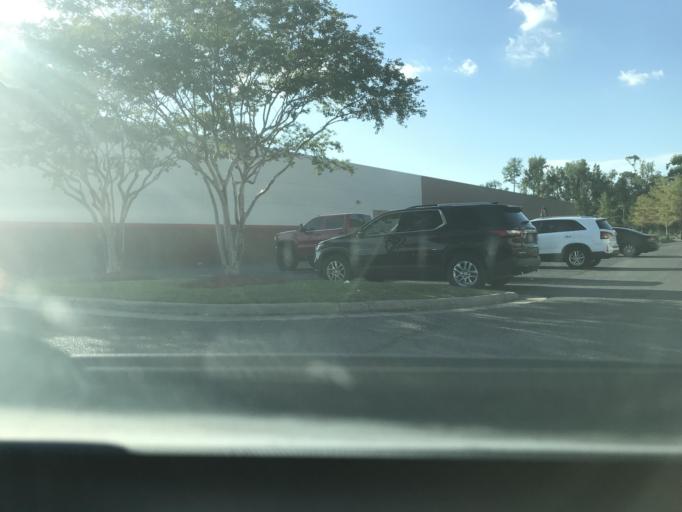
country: US
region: Louisiana
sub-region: Calcasieu Parish
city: Prien
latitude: 30.1996
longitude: -93.2455
